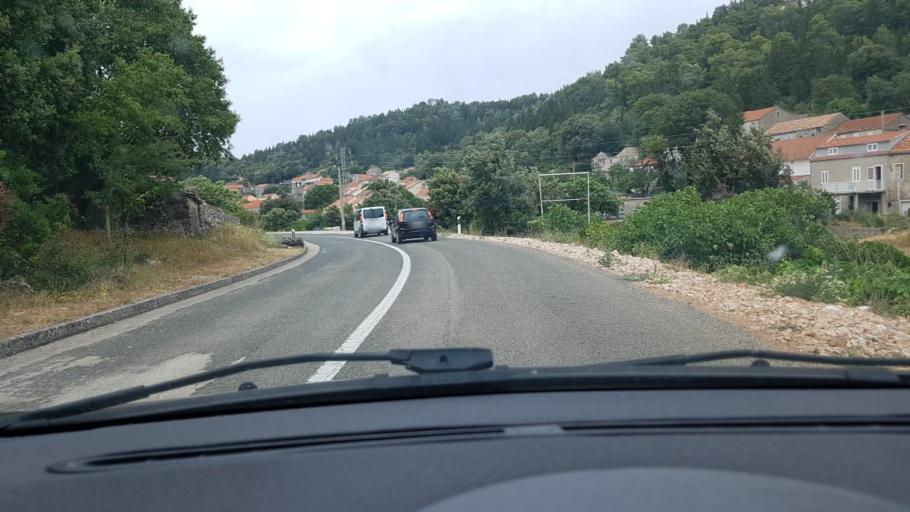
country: HR
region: Dubrovacko-Neretvanska
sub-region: Grad Korcula
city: Zrnovo
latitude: 42.9488
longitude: 17.0396
